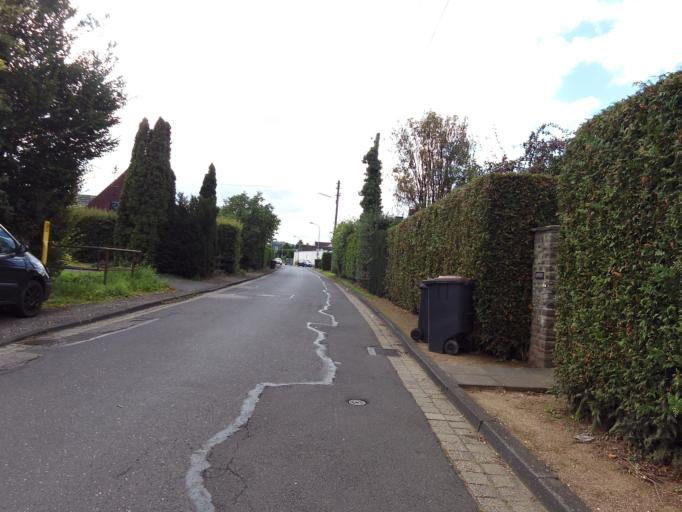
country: DE
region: North Rhine-Westphalia
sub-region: Regierungsbezirk Koln
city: Euskirchen
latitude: 50.6321
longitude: 6.8146
